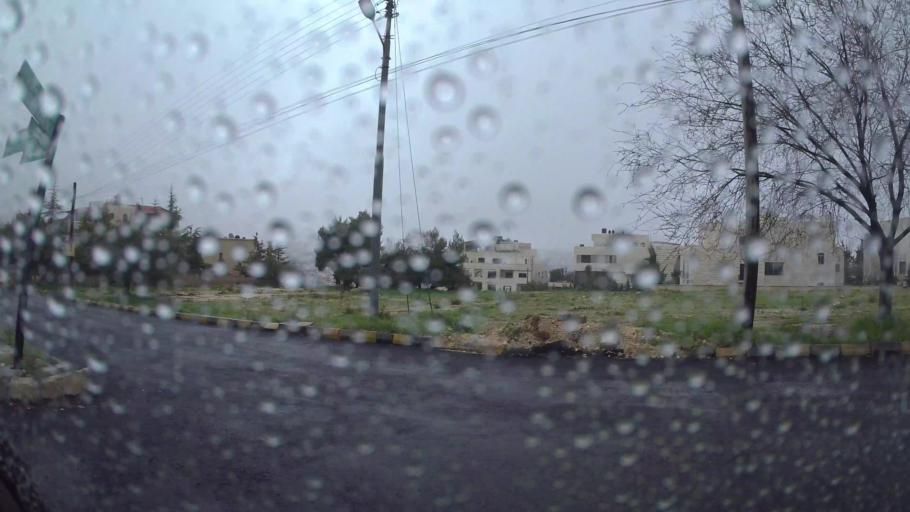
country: JO
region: Amman
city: Al Jubayhah
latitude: 32.0095
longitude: 35.8275
